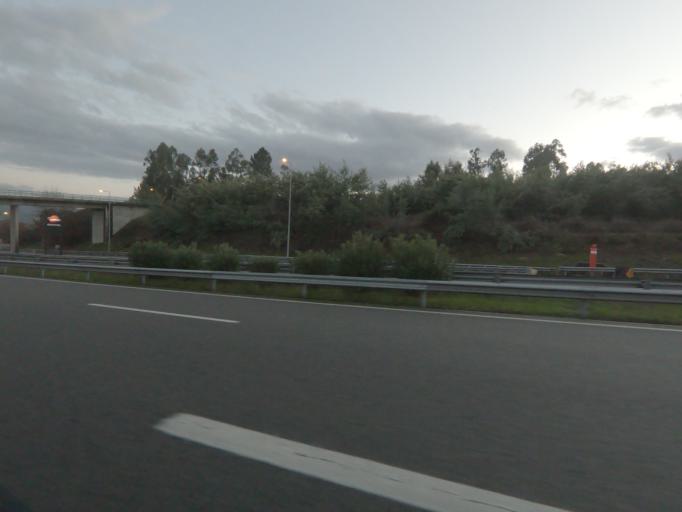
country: PT
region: Porto
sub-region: Marco de Canaveses
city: Marco de Canavezes
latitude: 41.2358
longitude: -8.1813
